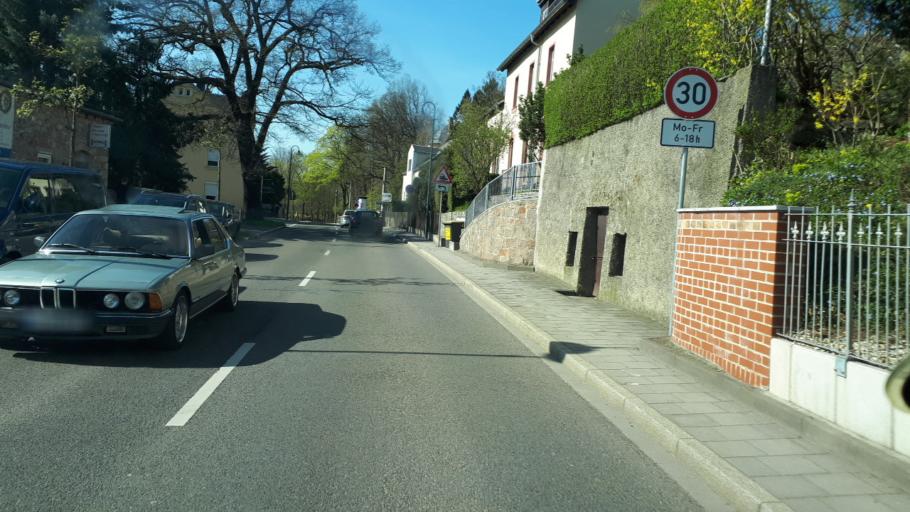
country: DE
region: Saxony
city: Chemnitz
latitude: 50.7881
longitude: 12.9506
